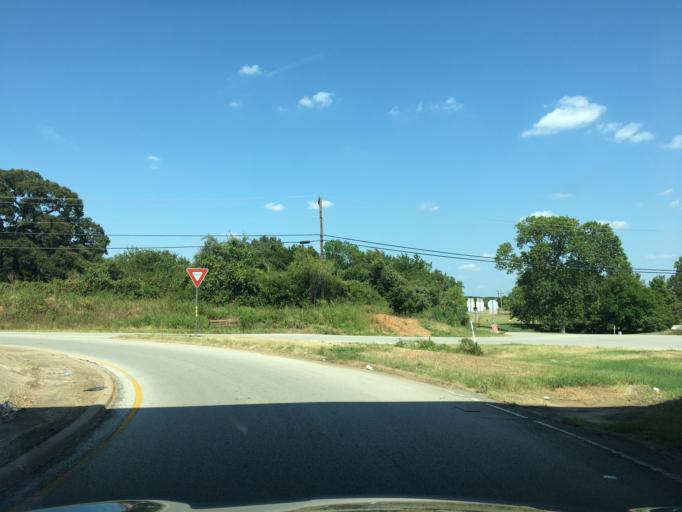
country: US
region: Texas
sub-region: Tarrant County
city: Kennedale
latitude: 32.6337
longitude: -97.1765
